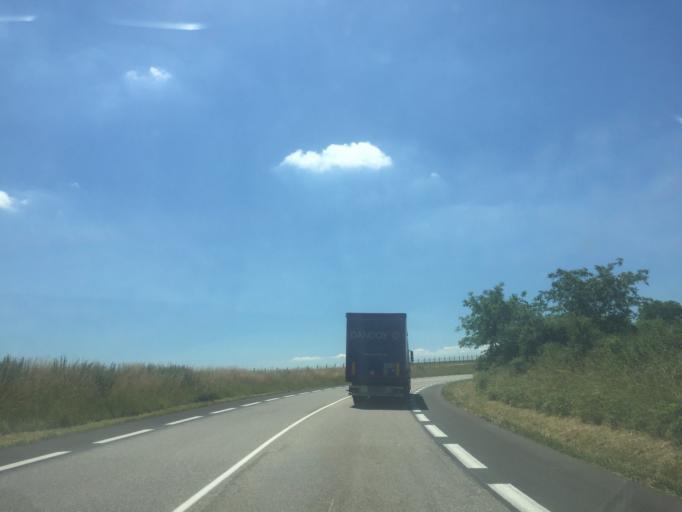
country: FR
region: Rhone-Alpes
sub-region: Departement du Rhone
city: Pusignan
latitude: 45.7455
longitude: 5.0810
